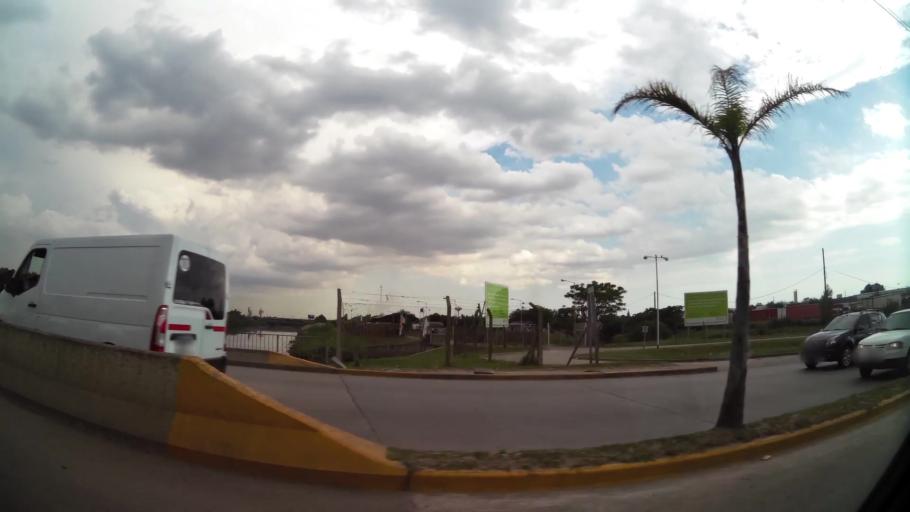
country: AR
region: Buenos Aires
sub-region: Partido de Tigre
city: Tigre
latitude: -34.4805
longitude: -58.6042
